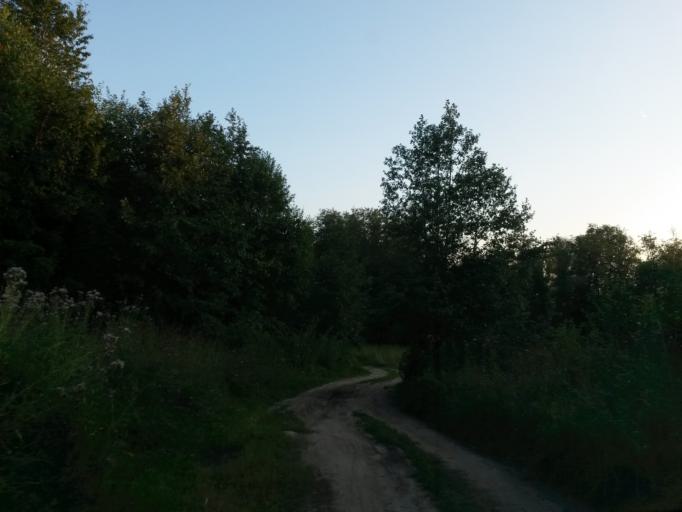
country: RU
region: Jaroslavl
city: Tutayev
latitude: 57.9357
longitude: 39.4461
